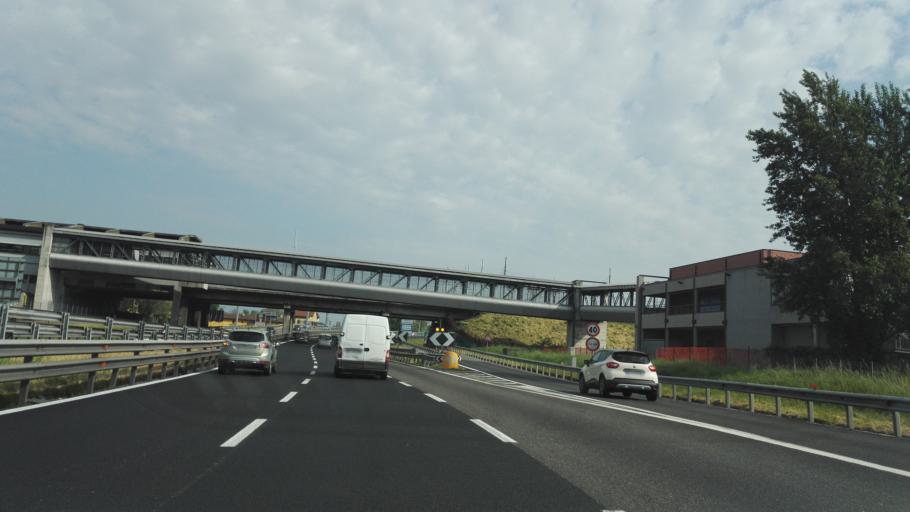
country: IT
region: Lombardy
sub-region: Citta metropolitana di Milano
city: Cologno Monzese
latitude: 45.5102
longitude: 9.2617
